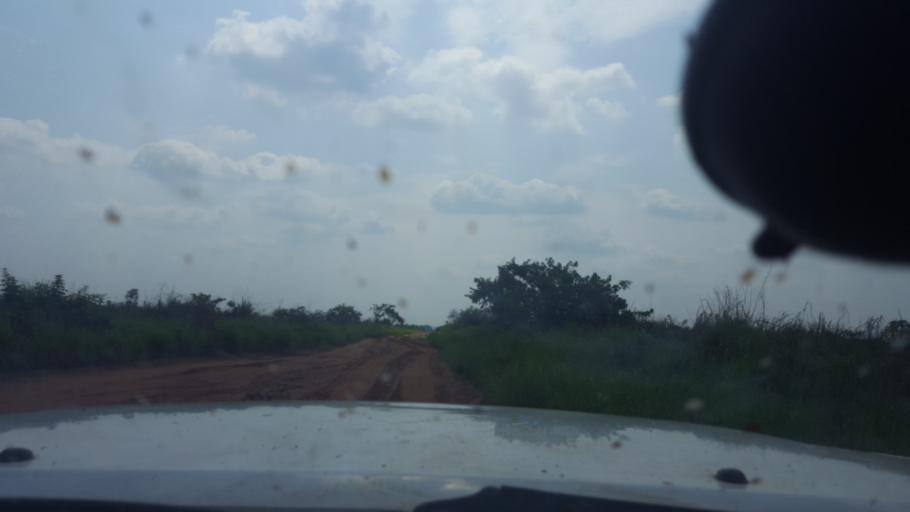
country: CD
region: Bandundu
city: Bandundu
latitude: -3.7615
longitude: 17.1312
